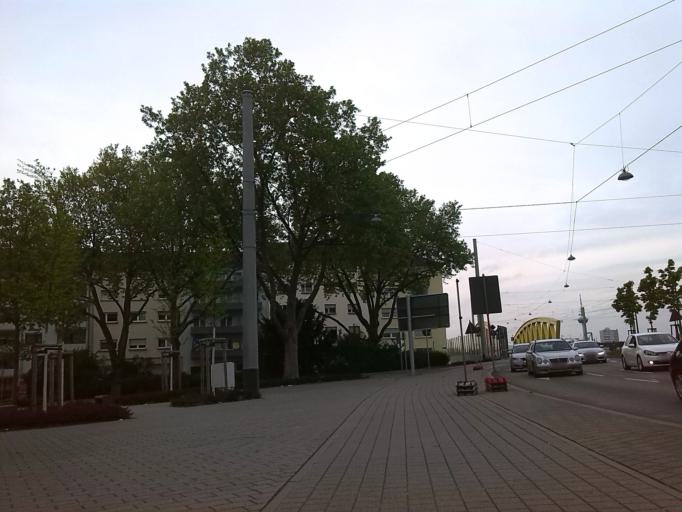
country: DE
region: Baden-Wuerttemberg
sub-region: Karlsruhe Region
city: Mannheim
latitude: 49.4694
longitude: 8.4836
